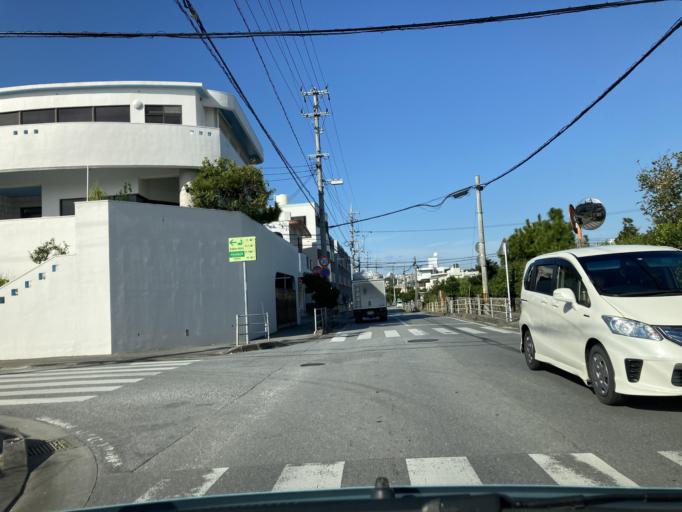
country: JP
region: Okinawa
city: Tomigusuku
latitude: 26.1816
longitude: 127.7068
